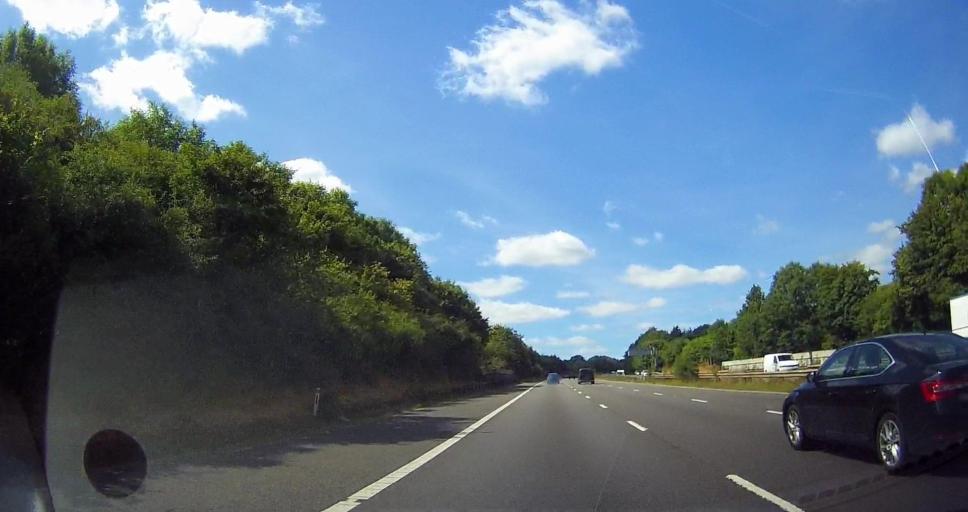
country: GB
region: England
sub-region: Worcestershire
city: Alvechurch
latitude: 52.3584
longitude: -1.9669
